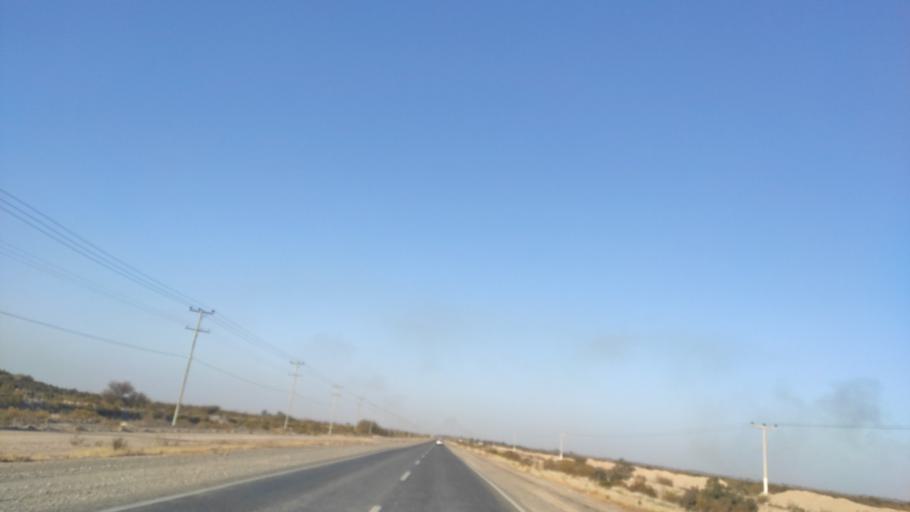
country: AR
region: San Juan
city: Villa Media Agua
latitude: -31.9783
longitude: -68.4981
